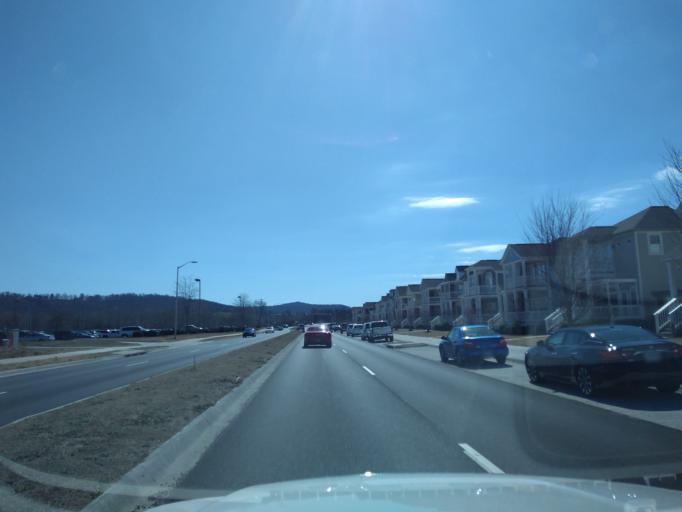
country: US
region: Arkansas
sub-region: Washington County
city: Farmington
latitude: 36.0739
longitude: -94.2176
